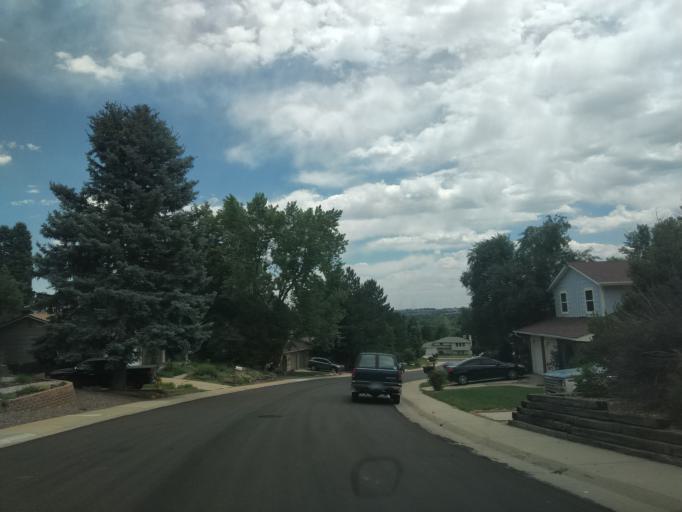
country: US
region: Colorado
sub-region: Jefferson County
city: Lakewood
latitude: 39.6732
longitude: -105.1019
